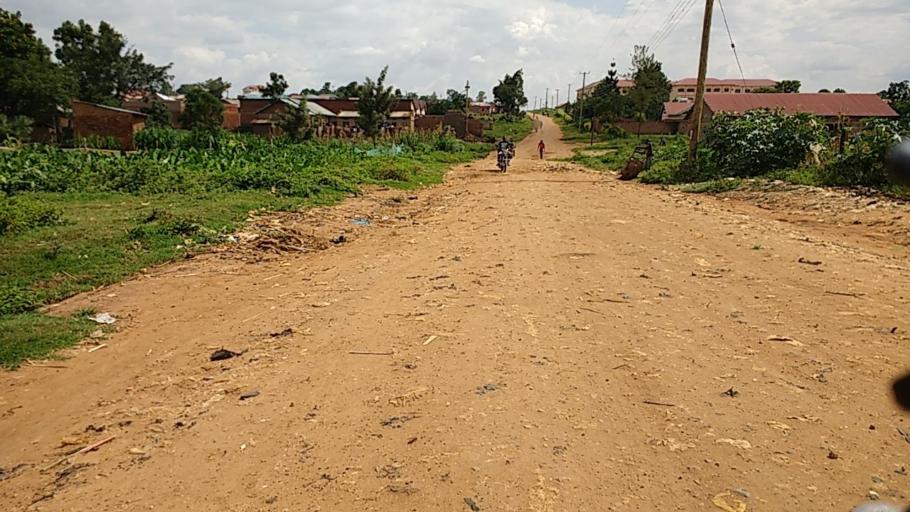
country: UG
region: Eastern Region
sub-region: Mbale District
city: Mbale
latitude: 1.0846
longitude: 34.1626
